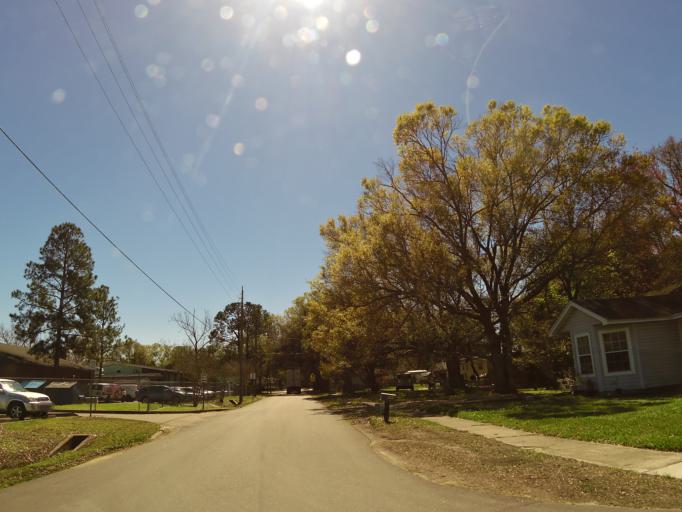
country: US
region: Florida
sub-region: Duval County
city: Jacksonville
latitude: 30.3240
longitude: -81.7225
